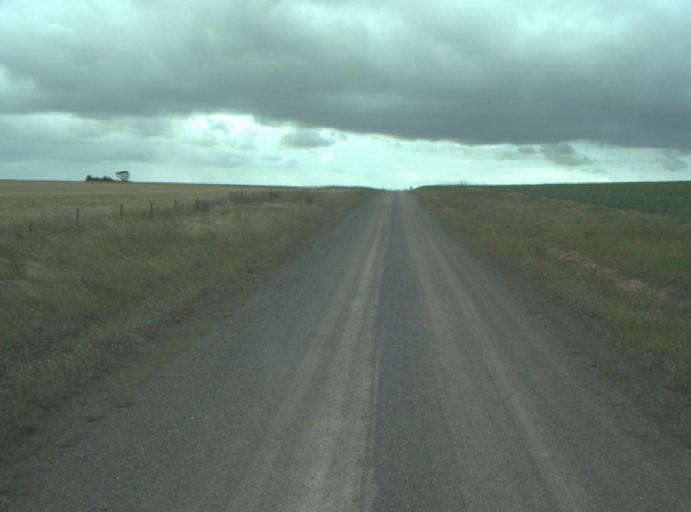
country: AU
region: Victoria
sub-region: Greater Geelong
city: Lara
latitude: -37.8875
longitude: 144.3502
